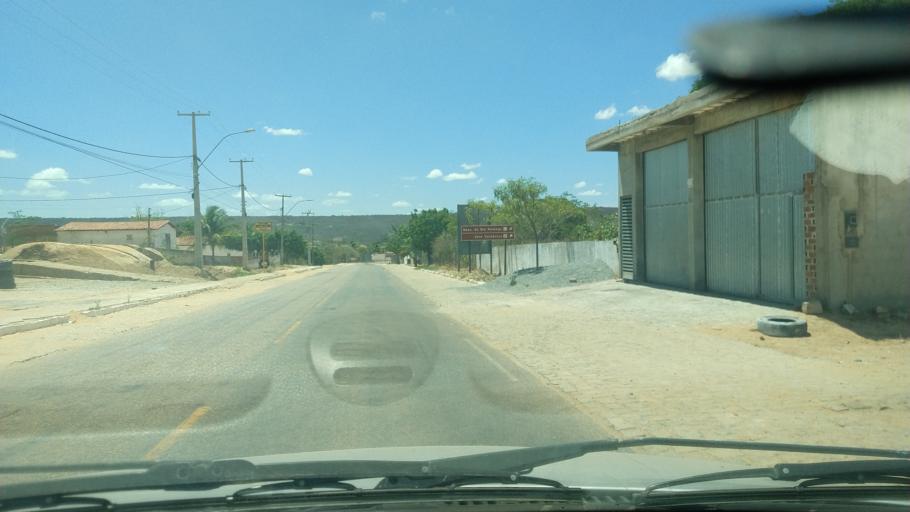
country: BR
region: Rio Grande do Norte
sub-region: Cerro Cora
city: Cerro Cora
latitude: -6.0546
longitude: -36.3570
